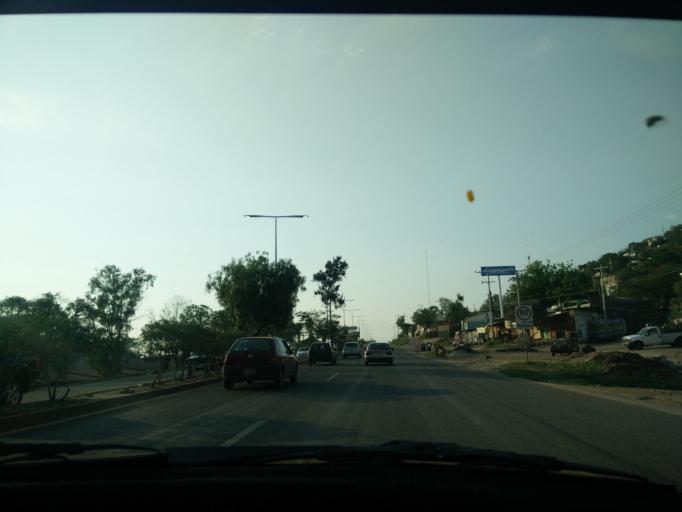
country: MX
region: Oaxaca
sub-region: Santa Maria Atzompa
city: San Jeronimo Yahuiche
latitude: 17.1059
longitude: -96.7536
